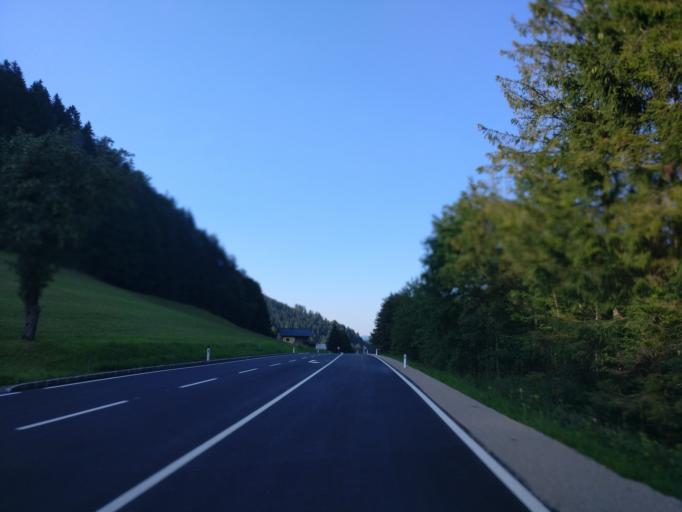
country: AT
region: Lower Austria
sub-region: Politischer Bezirk Scheibbs
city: Gostling an der Ybbs
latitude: 47.7478
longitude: 14.8981
